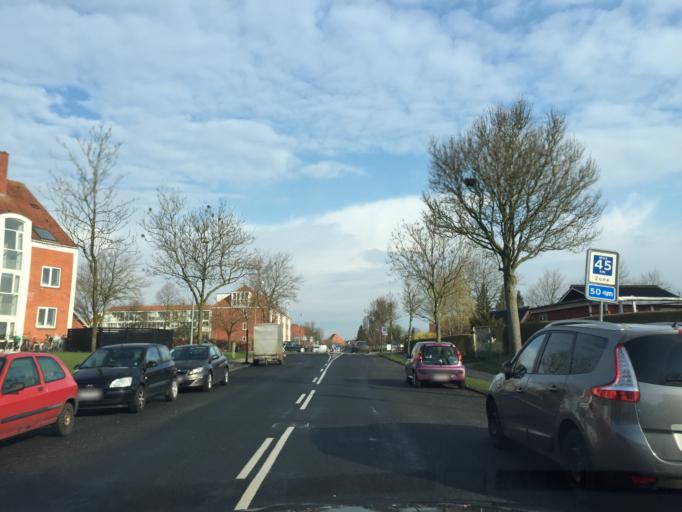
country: DK
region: South Denmark
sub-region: Odense Kommune
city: Odense
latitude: 55.3875
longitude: 10.4062
